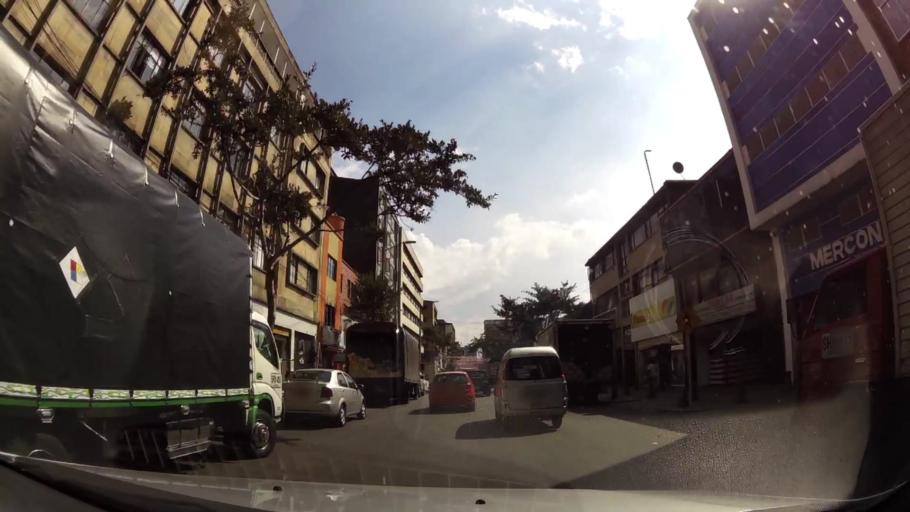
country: CO
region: Bogota D.C.
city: Bogota
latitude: 4.6070
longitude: -74.0761
